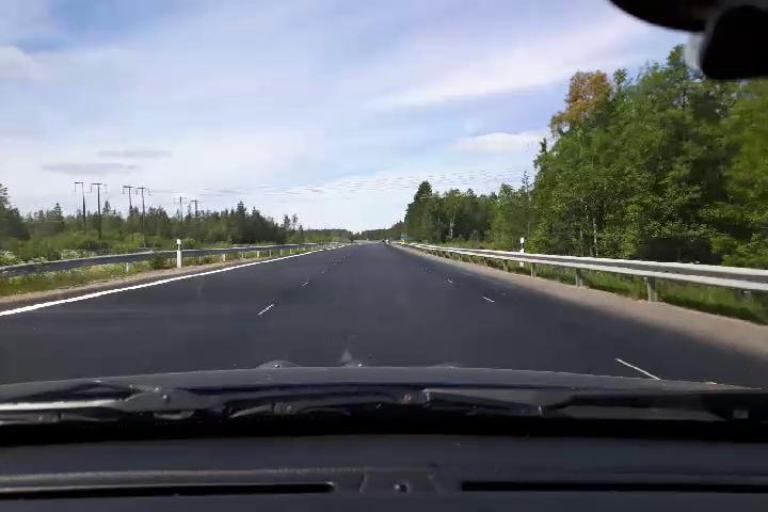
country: SE
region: Gaevleborg
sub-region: Gavle Kommun
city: Gavle
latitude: 60.6252
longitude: 17.1558
